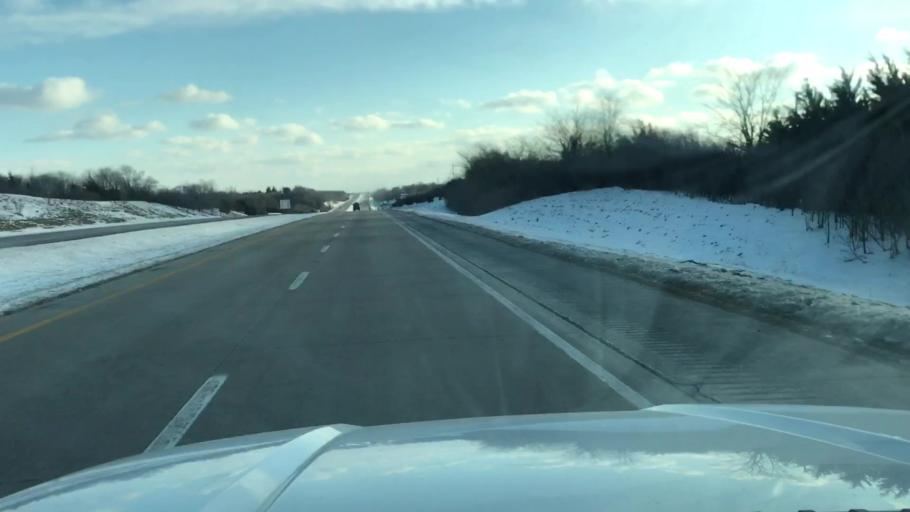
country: US
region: Missouri
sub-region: Andrew County
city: Savannah
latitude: 39.9470
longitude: -94.8603
